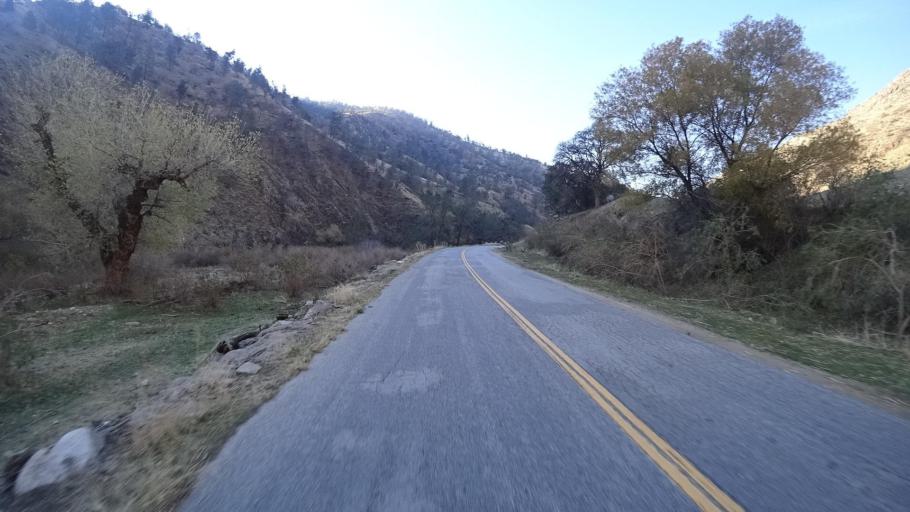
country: US
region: California
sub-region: Kern County
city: Bear Valley Springs
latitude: 35.3174
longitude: -118.5419
